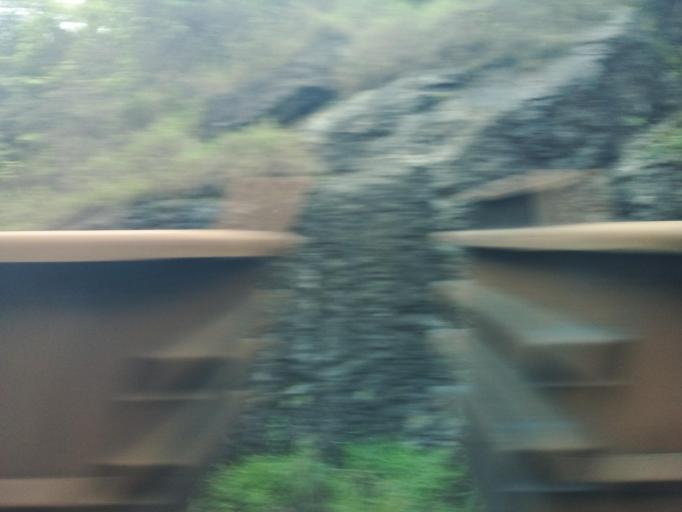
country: BR
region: Minas Gerais
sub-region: Rio Piracicaba
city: Rio Piracicaba
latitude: -19.9693
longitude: -43.2507
